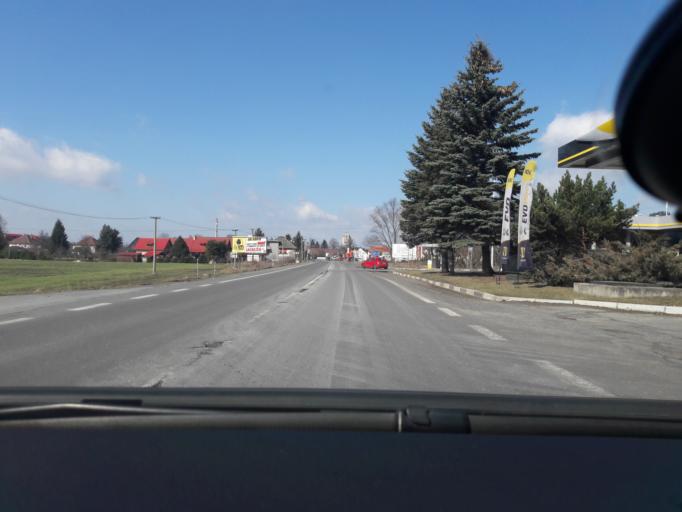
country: SK
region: Zilinsky
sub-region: Okres Liptovsky Mikulas
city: Liptovsky Mikulas
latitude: 49.0740
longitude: 19.6585
